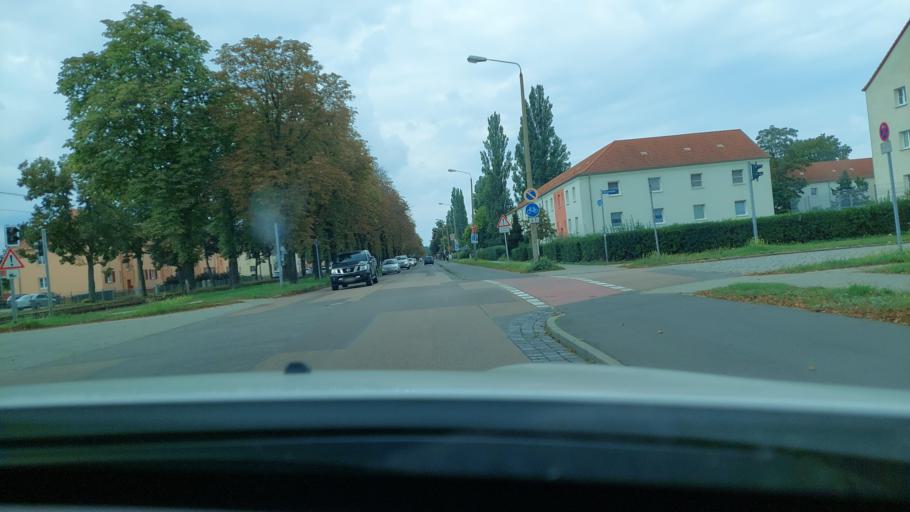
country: DE
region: Brandenburg
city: Brandenburg an der Havel
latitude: 52.4253
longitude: 12.5179
